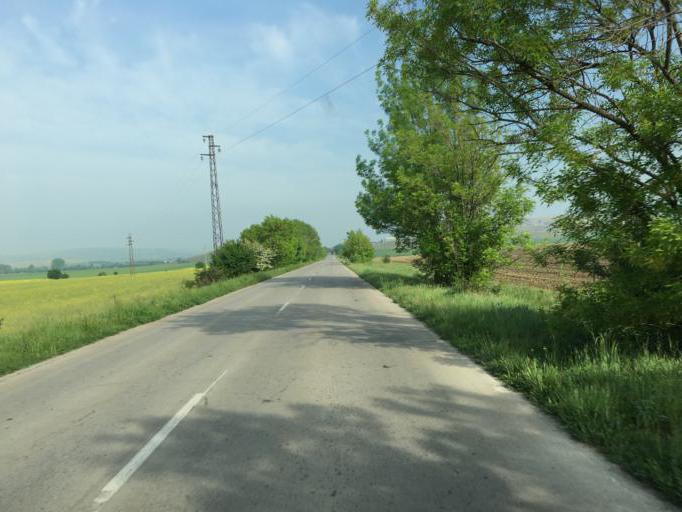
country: BG
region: Pernik
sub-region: Obshtina Radomir
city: Radomir
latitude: 42.4897
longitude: 23.0457
